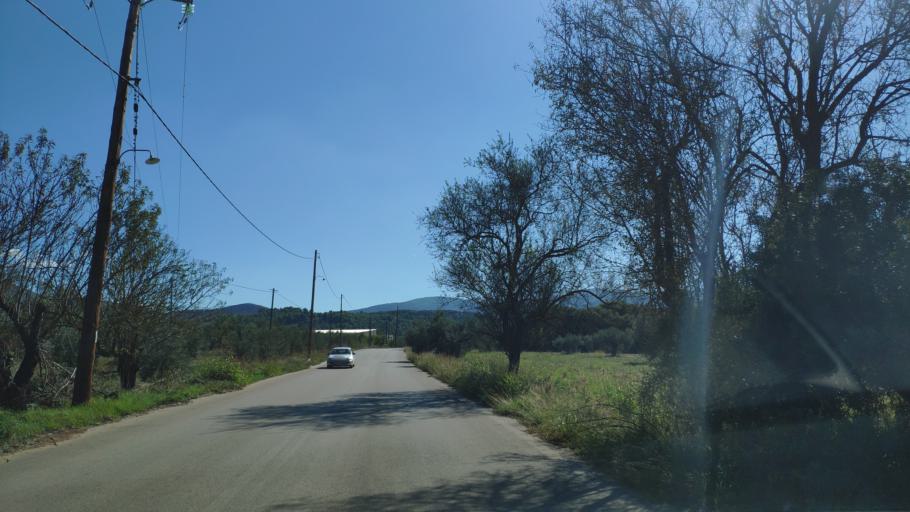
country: GR
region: Peloponnese
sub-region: Nomos Korinthias
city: Athikia
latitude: 37.8394
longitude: 22.9104
